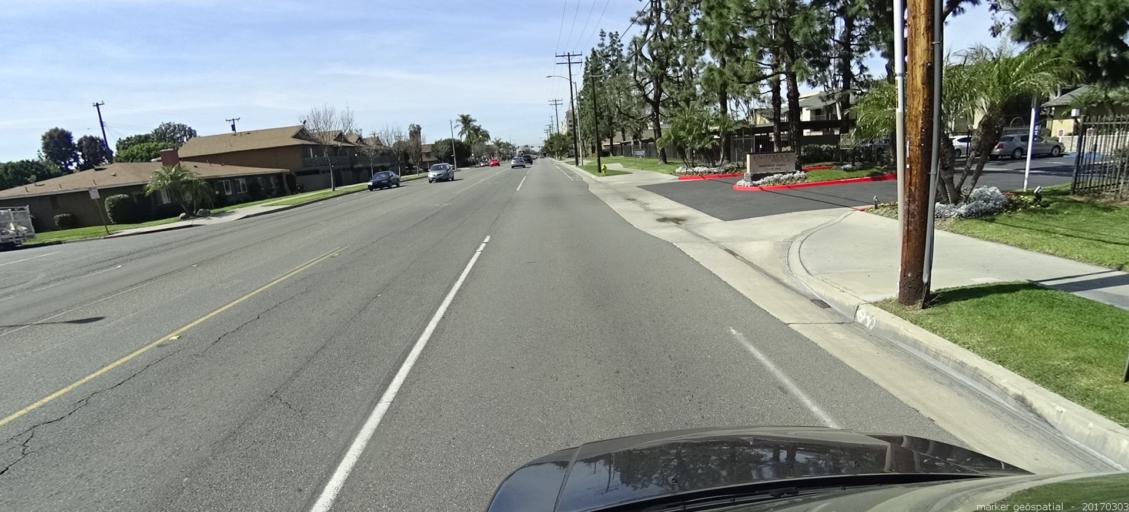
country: US
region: California
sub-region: Orange County
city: Garden Grove
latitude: 33.7962
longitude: -117.9116
